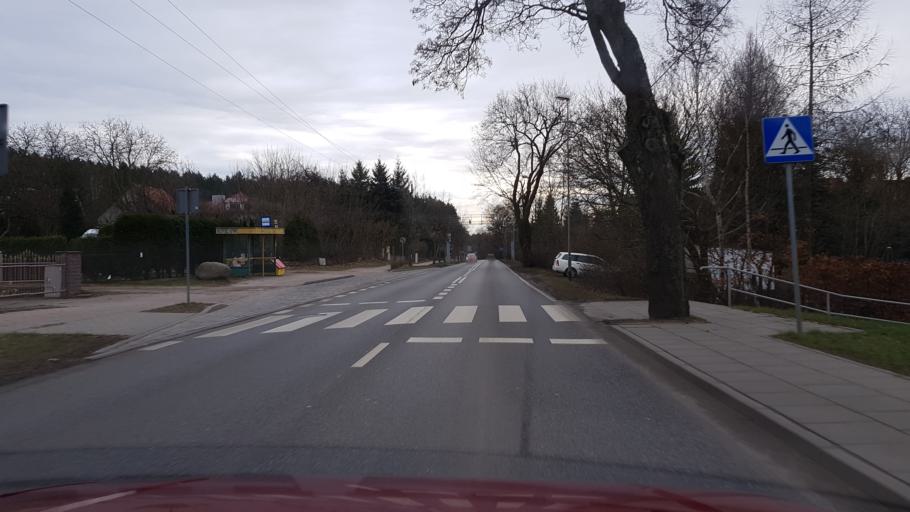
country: PL
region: West Pomeranian Voivodeship
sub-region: Powiat policki
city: Dobra
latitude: 53.4936
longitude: 14.4807
